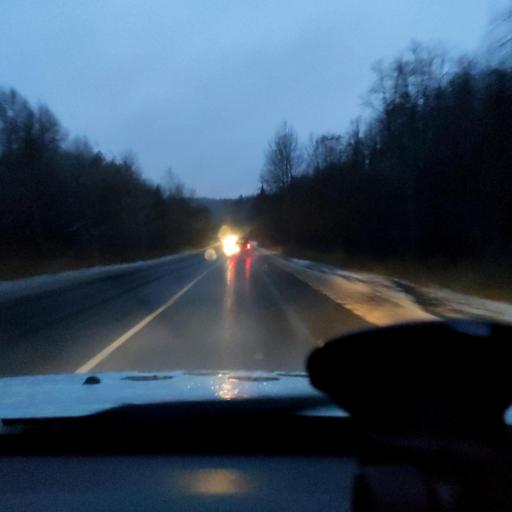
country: RU
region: Perm
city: Ferma
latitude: 57.9587
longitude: 56.3321
